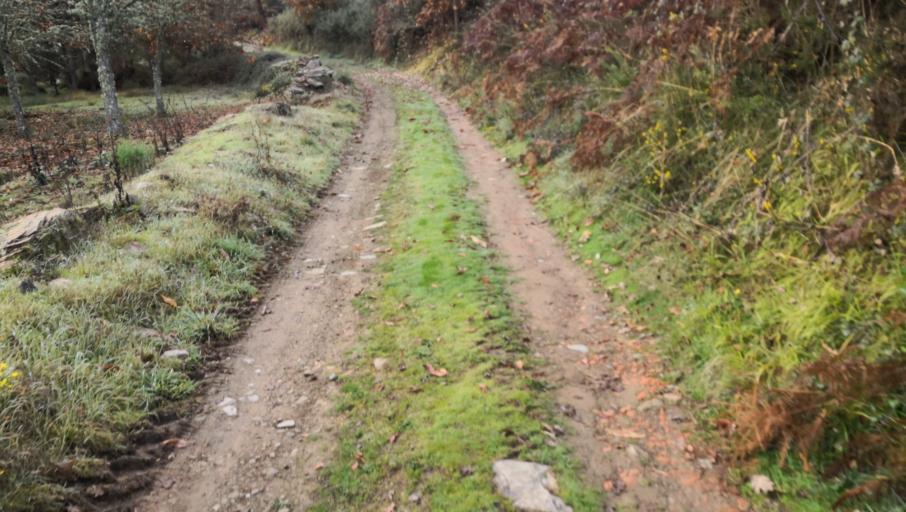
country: PT
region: Vila Real
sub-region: Sabrosa
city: Vilela
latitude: 41.2550
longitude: -7.6314
